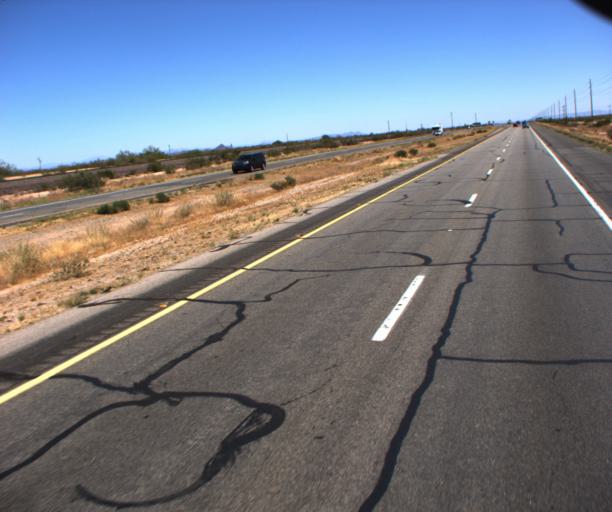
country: US
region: Arizona
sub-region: Maricopa County
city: Sun City West
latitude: 33.7586
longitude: -112.5041
